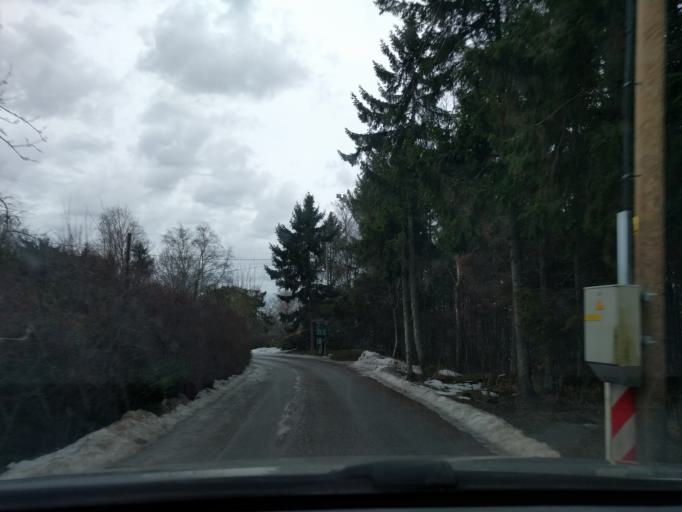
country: EE
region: Harju
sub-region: Viimsi vald
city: Viimsi
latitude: 59.5140
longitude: 24.9059
